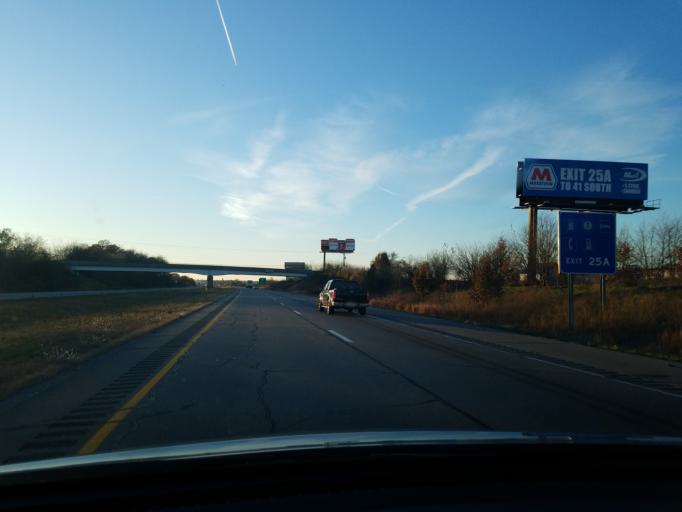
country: US
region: Indiana
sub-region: Gibson County
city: Haubstadt
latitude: 38.1668
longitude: -87.5289
